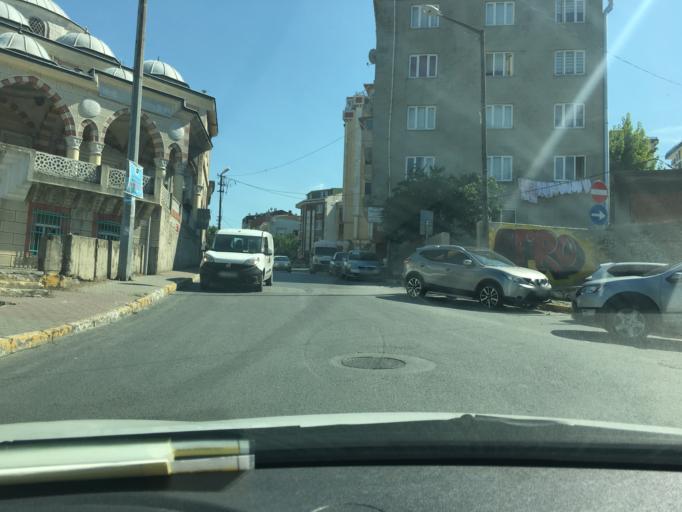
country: TR
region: Istanbul
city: Sisli
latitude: 41.0822
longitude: 28.9443
